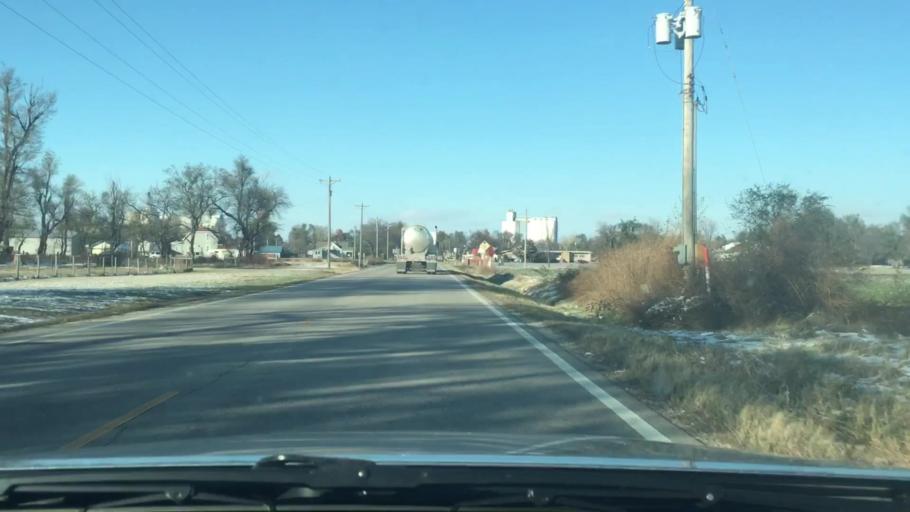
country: US
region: Kansas
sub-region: Rice County
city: Sterling
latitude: 38.1999
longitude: -98.2068
